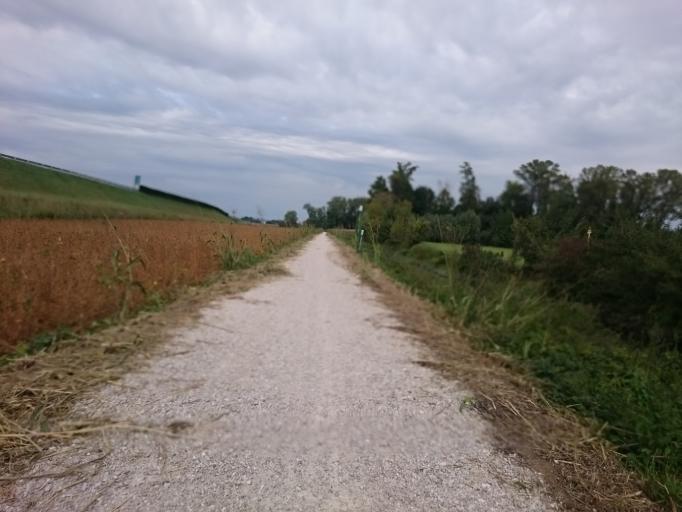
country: IT
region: Veneto
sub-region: Provincia di Vicenza
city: Grisignano di Zocco
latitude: 45.4864
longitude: 11.6846
